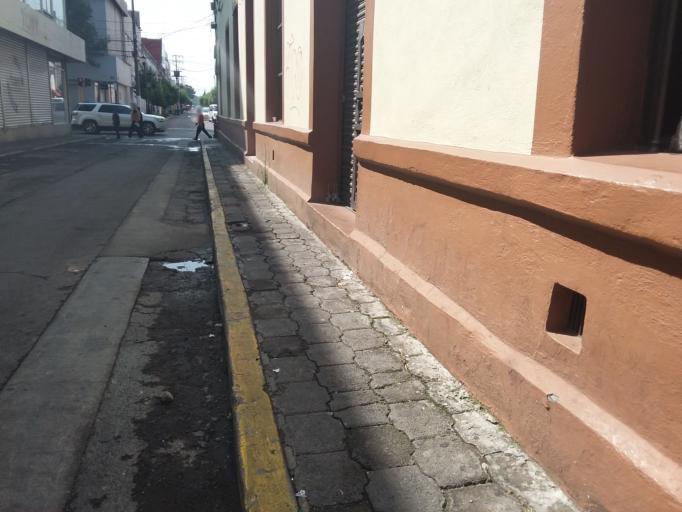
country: MX
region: Mexico
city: Toluca
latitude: 19.2906
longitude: -99.6551
